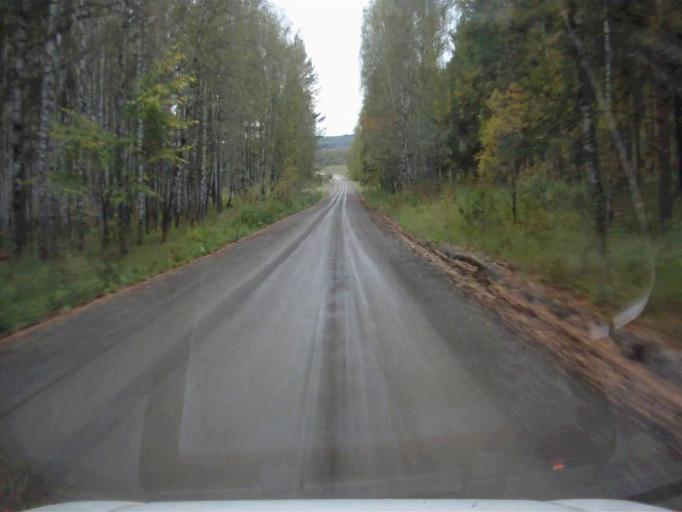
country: RU
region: Chelyabinsk
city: Nyazepetrovsk
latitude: 56.1223
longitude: 59.3605
